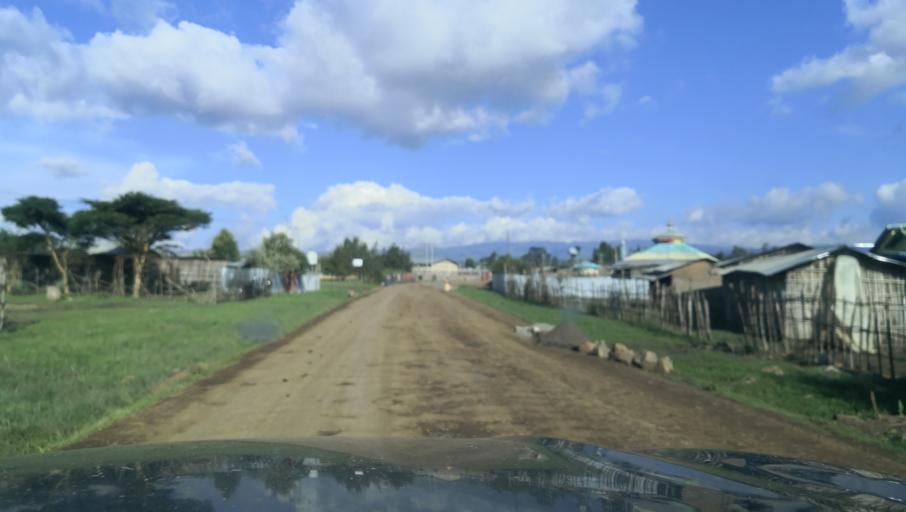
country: ET
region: Oromiya
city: Tulu Bolo
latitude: 8.4740
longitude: 38.2464
